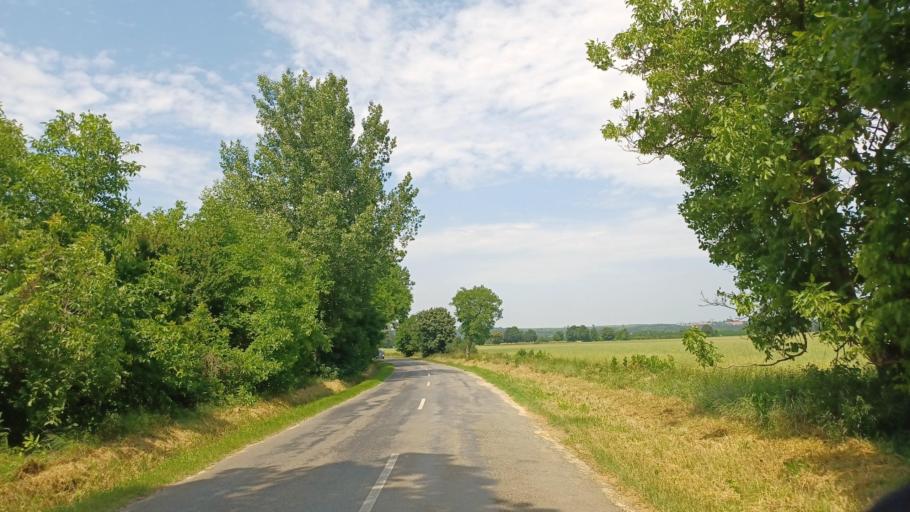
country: HU
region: Tolna
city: Simontornya
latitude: 46.7235
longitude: 18.4957
